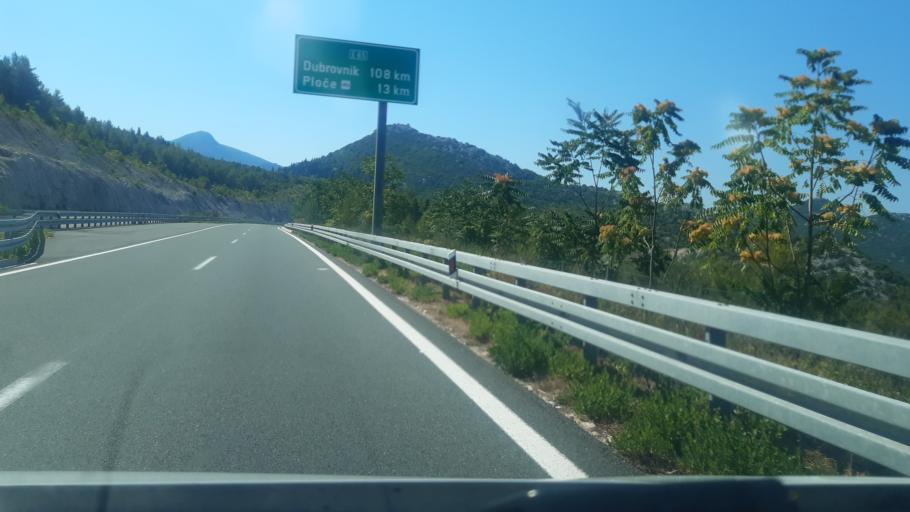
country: BA
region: Federation of Bosnia and Herzegovina
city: Ljubuski
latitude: 43.1346
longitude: 17.4833
